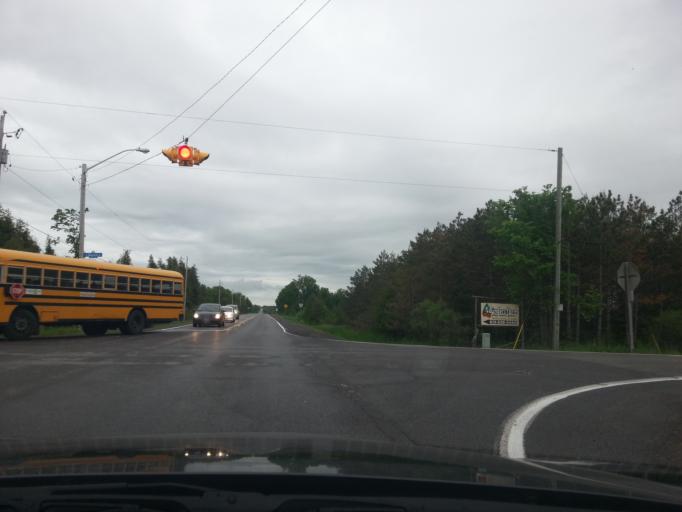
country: CA
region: Ontario
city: Bells Corners
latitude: 45.1836
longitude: -75.9616
